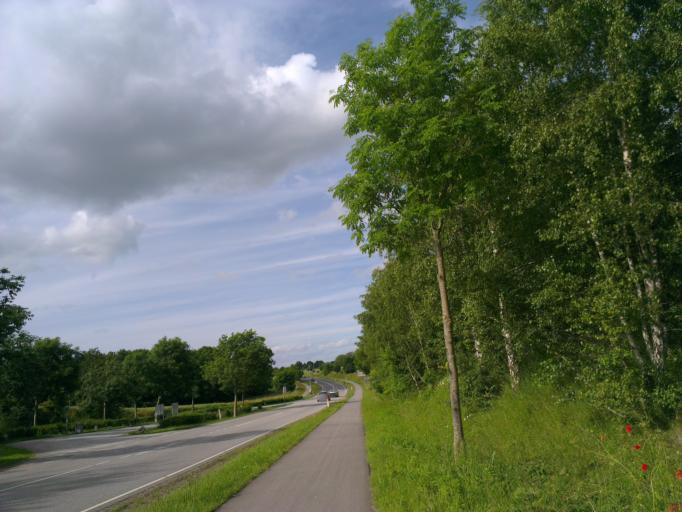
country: DK
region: Capital Region
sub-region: Frederikssund Kommune
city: Skibby
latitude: 55.7367
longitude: 11.9494
